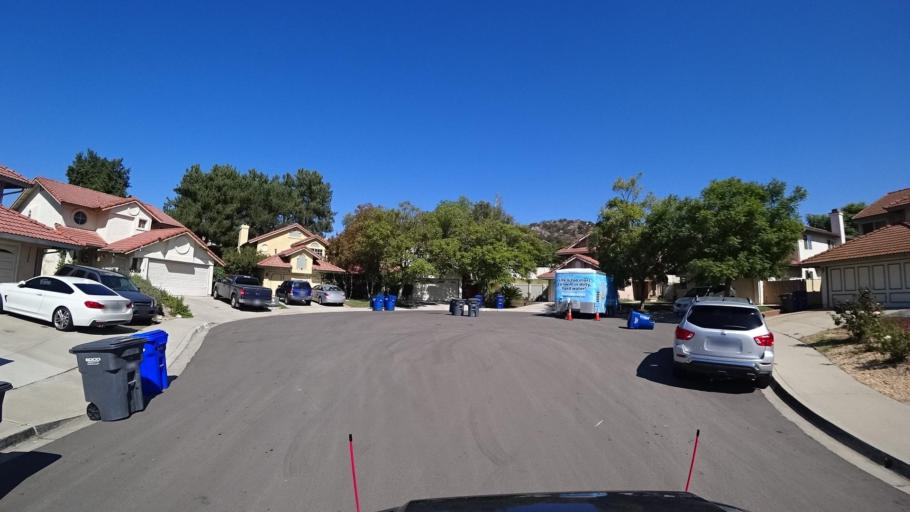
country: US
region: California
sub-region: San Diego County
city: Rancho San Diego
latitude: 32.7548
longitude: -116.9344
